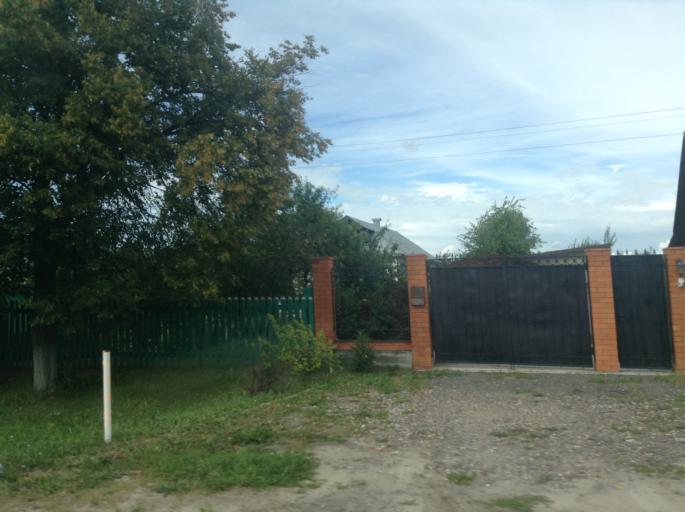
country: RU
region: Moskovskaya
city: Yegor'yevsk
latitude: 55.3530
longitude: 39.1280
